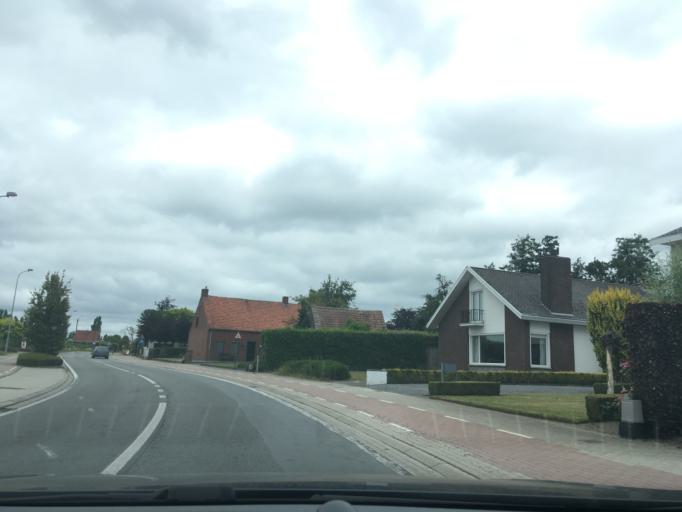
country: BE
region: Flanders
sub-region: Provincie West-Vlaanderen
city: Wingene
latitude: 51.0650
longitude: 3.2824
